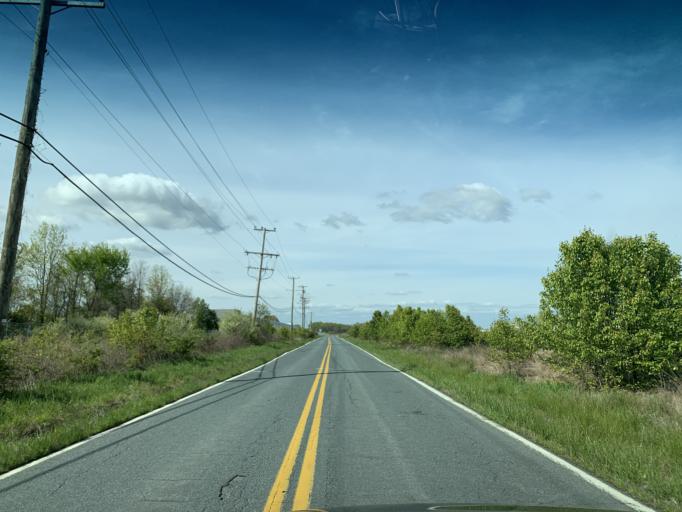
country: US
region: Maryland
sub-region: Harford County
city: Perryman
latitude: 39.4448
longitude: -76.2147
